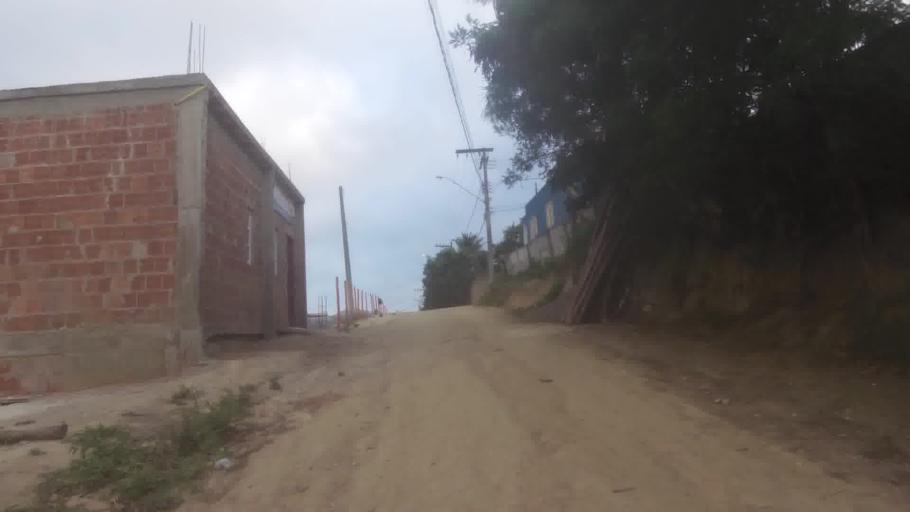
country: BR
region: Espirito Santo
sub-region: Itapemirim
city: Itapemirim
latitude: -21.0208
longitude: -40.8198
